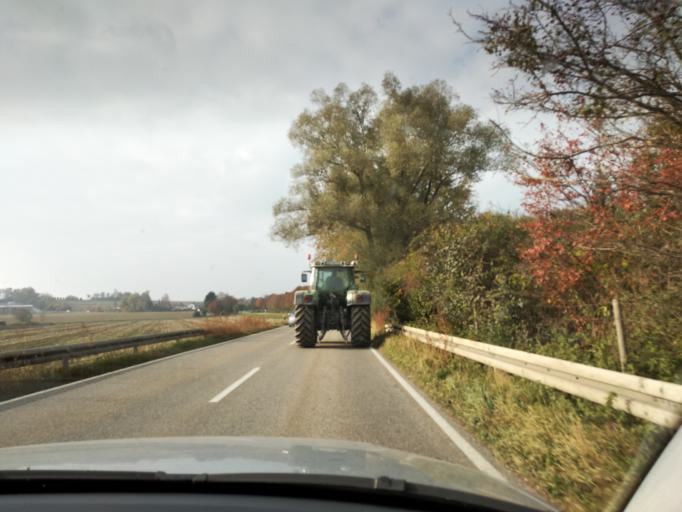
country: DE
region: Bavaria
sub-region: Upper Bavaria
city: Markt Schwaben
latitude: 48.1811
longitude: 11.8771
